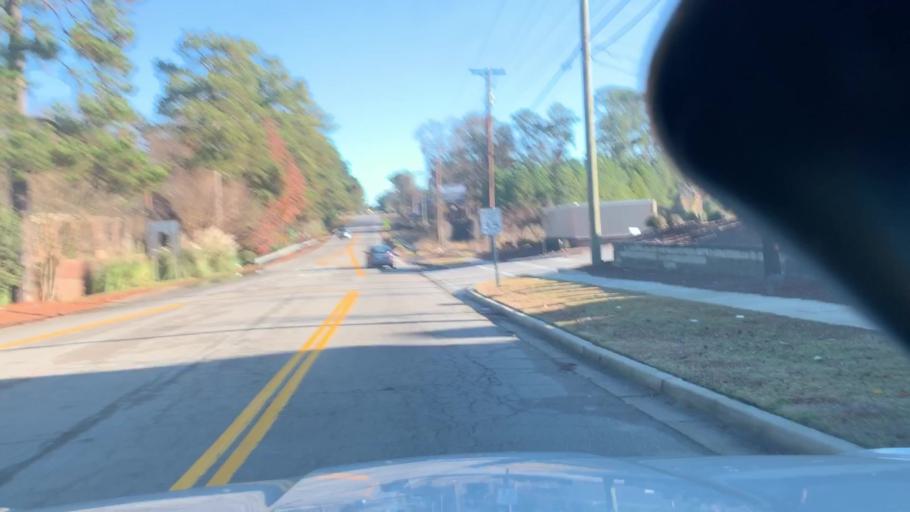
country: US
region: South Carolina
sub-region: Richland County
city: Forest Acres
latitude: 34.0243
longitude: -80.9509
